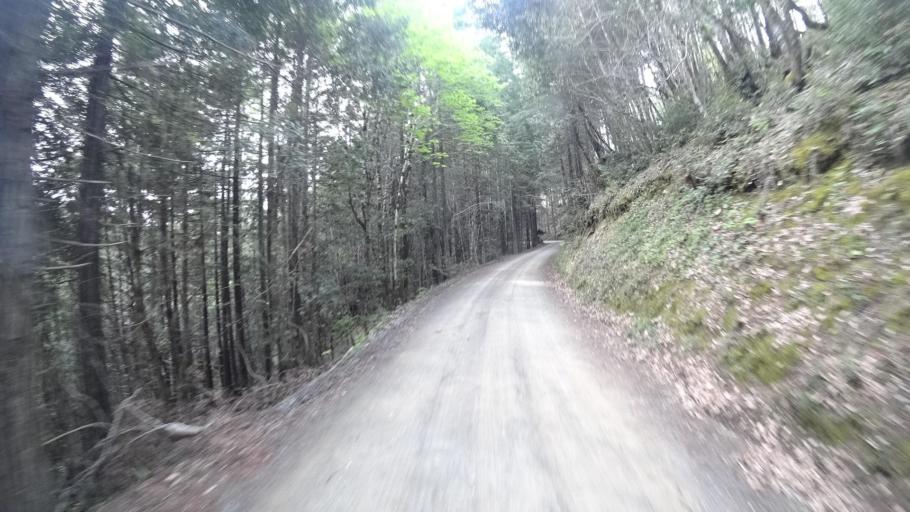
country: US
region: California
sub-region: Humboldt County
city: Redway
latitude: 40.3126
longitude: -123.8222
